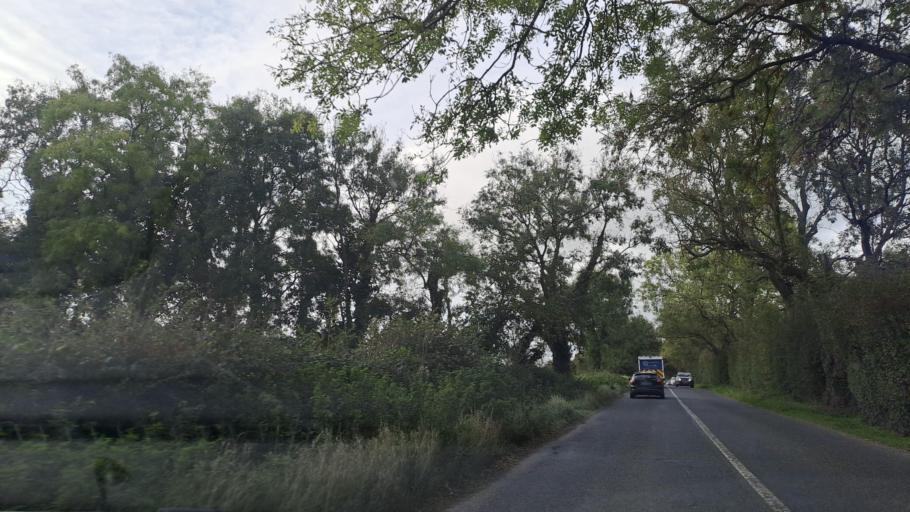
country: IE
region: Leinster
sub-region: An Mhi
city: Navan
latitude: 53.7236
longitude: -6.7029
